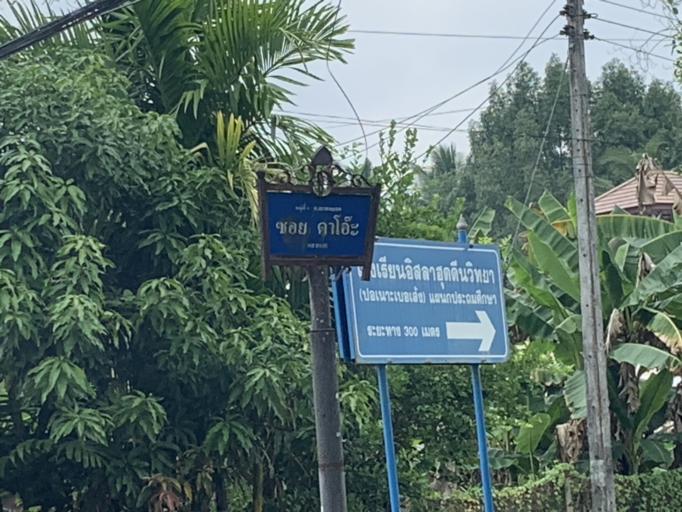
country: TH
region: Yala
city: Yala
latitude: 6.5208
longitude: 101.2889
